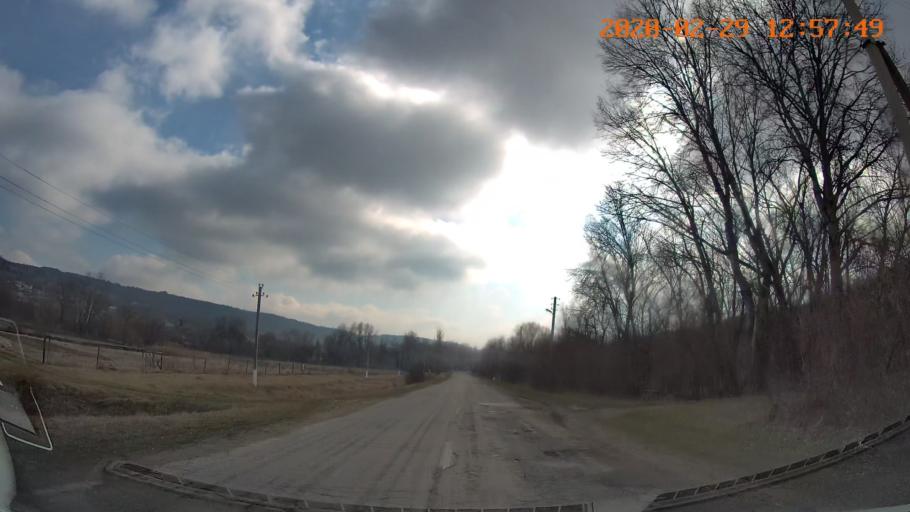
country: MD
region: Telenesti
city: Camenca
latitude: 48.0743
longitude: 28.7169
